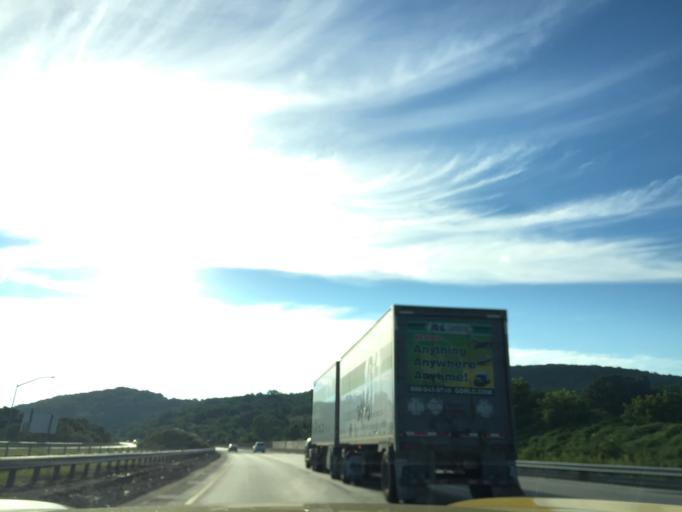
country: US
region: Pennsylvania
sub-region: Northampton County
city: Hellertown
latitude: 40.5953
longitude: -75.3304
